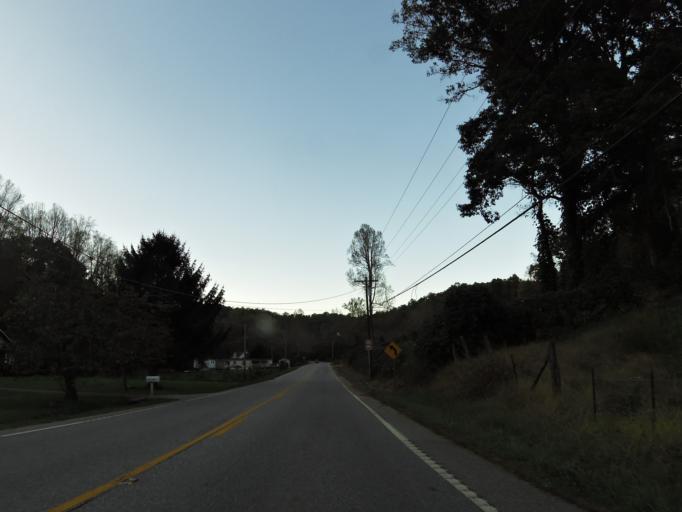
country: US
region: Tennessee
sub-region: Campbell County
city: Caryville
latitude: 36.2653
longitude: -84.1874
